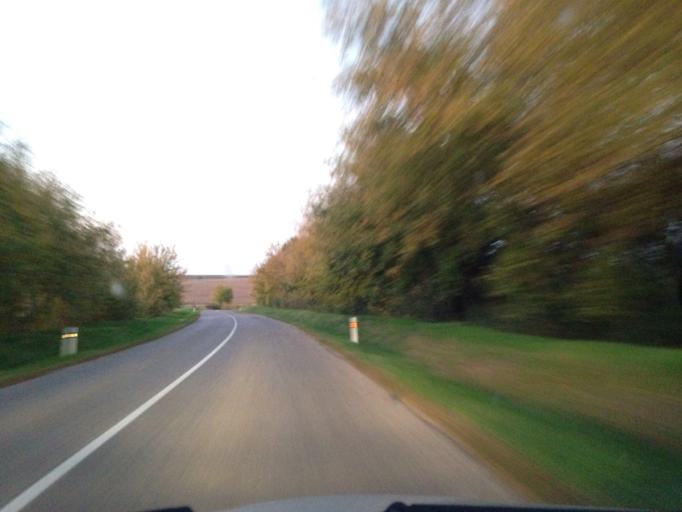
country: SK
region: Nitriansky
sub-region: Okres Komarno
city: Hurbanovo
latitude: 47.8763
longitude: 18.2858
